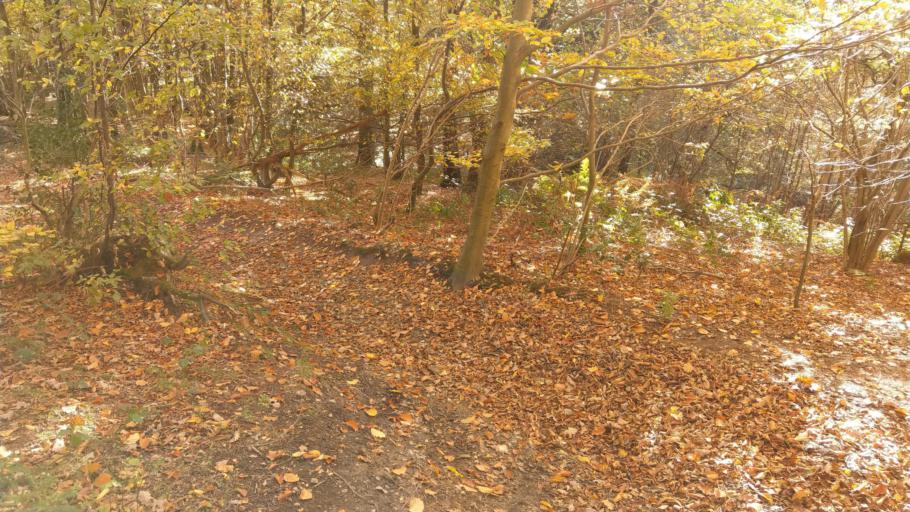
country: NL
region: Limburg
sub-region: Gemeente Vaals
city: Vaals
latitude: 50.7536
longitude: 6.0159
